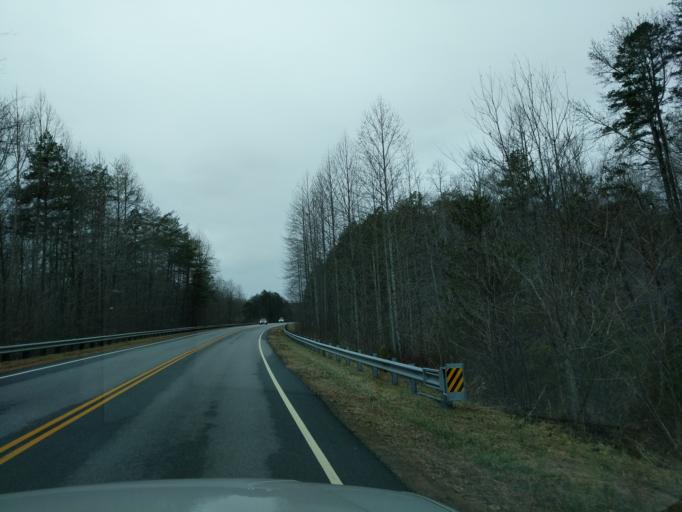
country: US
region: South Carolina
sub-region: Greenville County
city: Slater-Marietta
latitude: 35.0836
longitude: -82.4812
